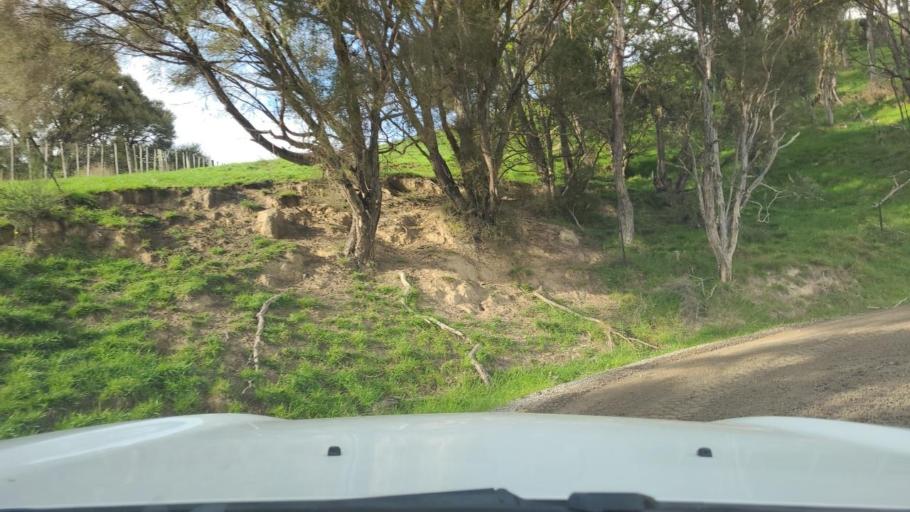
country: NZ
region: Wellington
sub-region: South Wairarapa District
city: Waipawa
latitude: -41.2309
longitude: 175.6829
